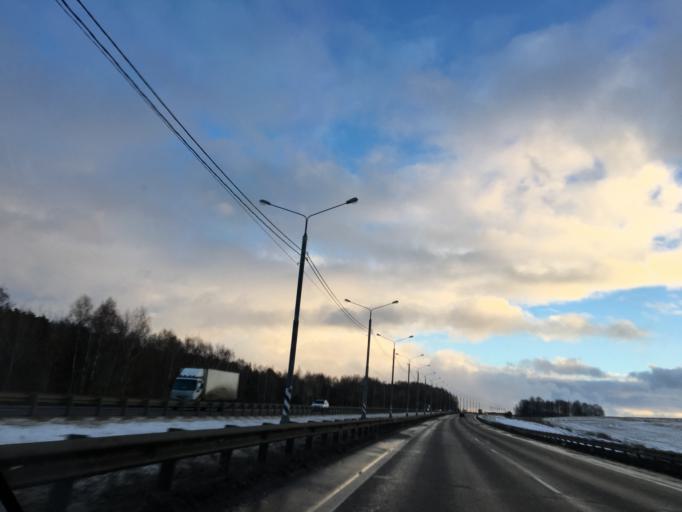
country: RU
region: Tula
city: Zaokskiy
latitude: 54.8178
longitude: 37.4768
